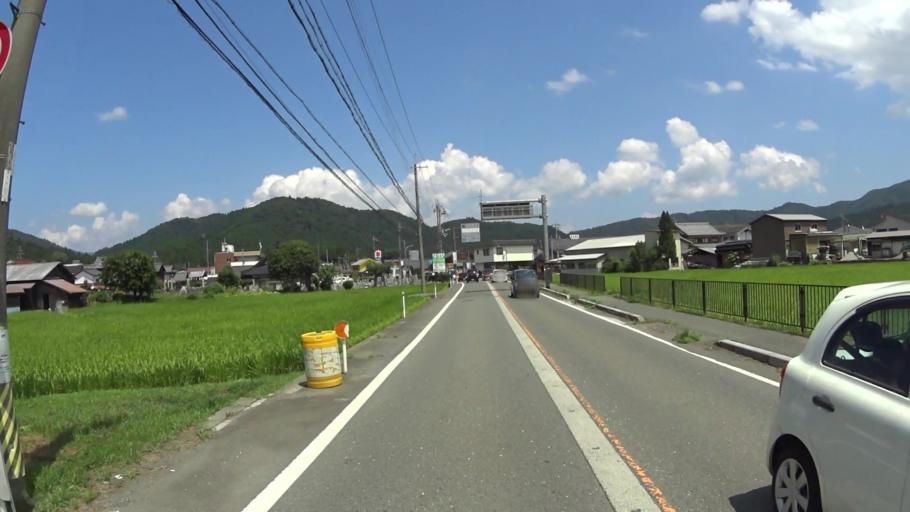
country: JP
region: Shiga Prefecture
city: Kitahama
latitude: 35.3524
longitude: 135.9162
